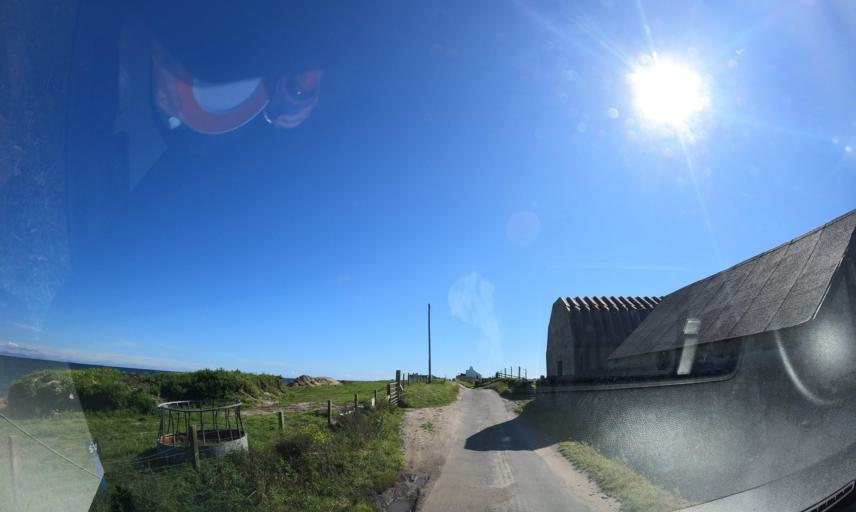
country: GB
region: Scotland
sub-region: Eilean Siar
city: Barra
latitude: 56.4638
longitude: -6.8948
